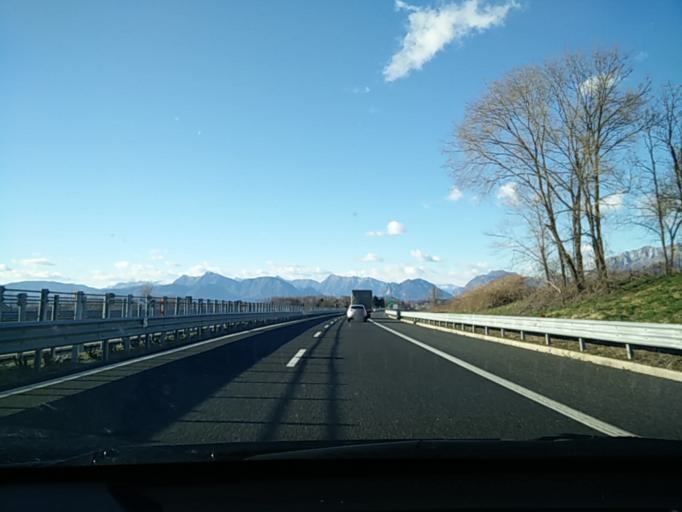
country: IT
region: Friuli Venezia Giulia
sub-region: Provincia di Udine
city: Pagnacco
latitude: 46.1406
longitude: 13.1757
